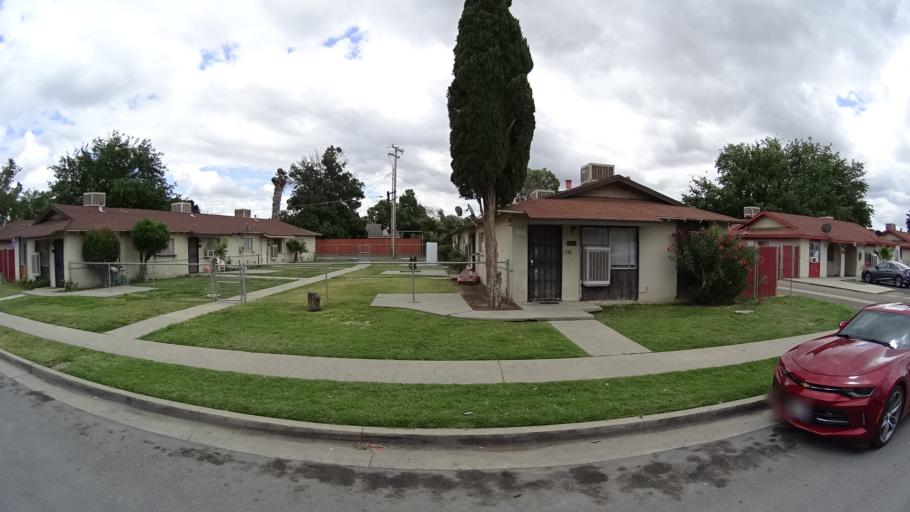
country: US
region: California
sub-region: Kings County
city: Hanford
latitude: 36.3366
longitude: -119.6264
